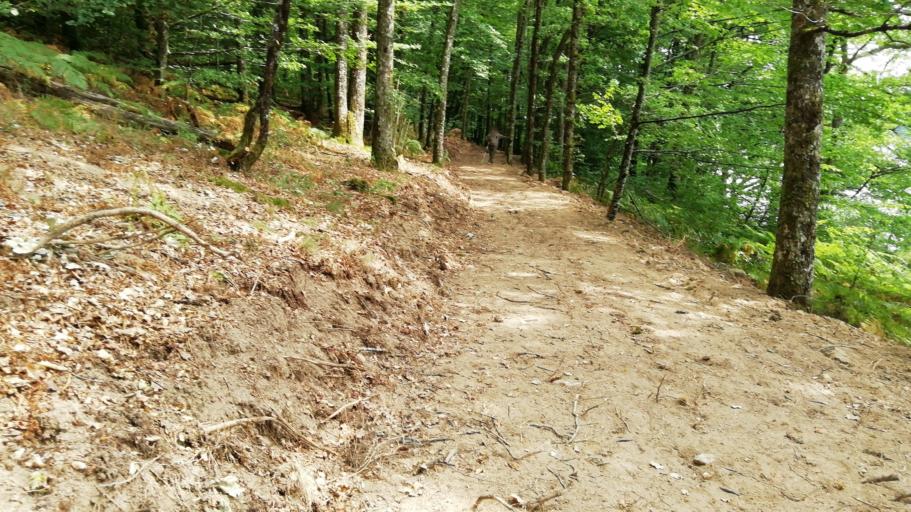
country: FR
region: Auvergne
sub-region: Departement du Cantal
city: Laroquebrou
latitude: 44.9463
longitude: 2.2295
